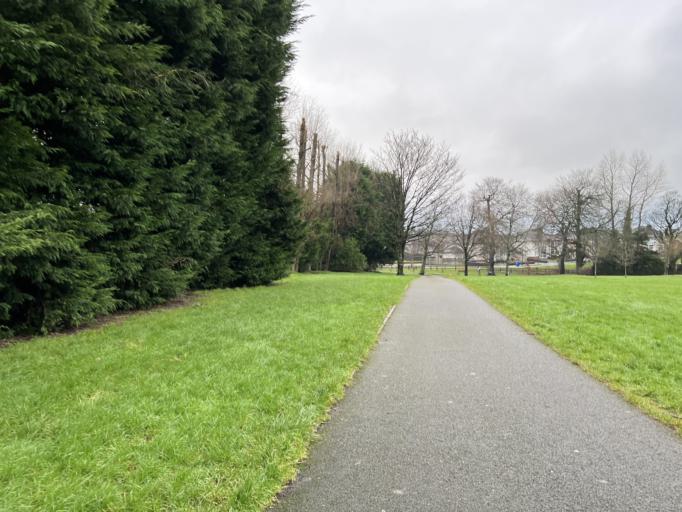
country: IE
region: Connaught
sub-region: County Galway
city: Tuam
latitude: 53.5205
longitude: -8.8499
